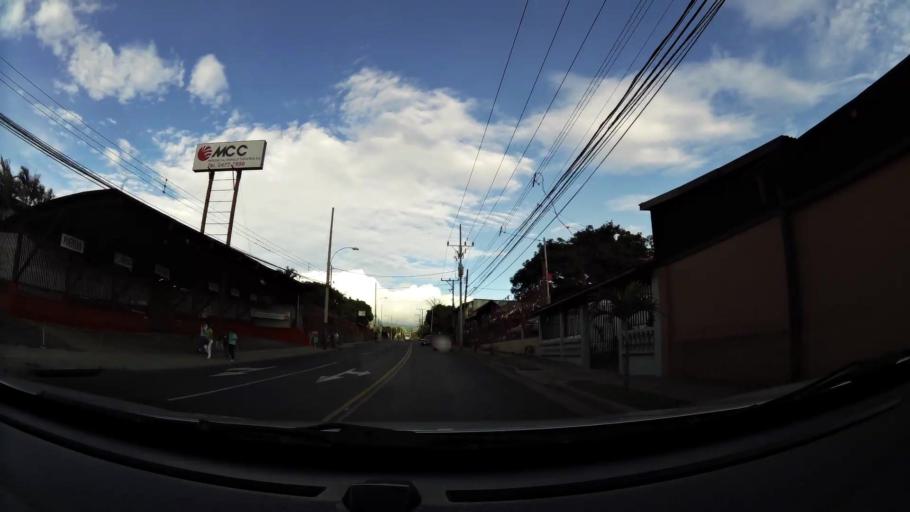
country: CR
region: Heredia
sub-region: Canton de Belen
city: San Antonio
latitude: 10.0044
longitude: -84.1827
